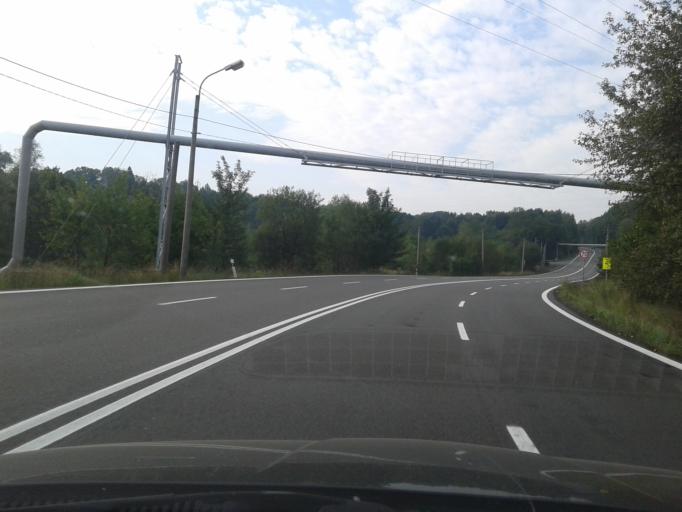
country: CZ
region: Moravskoslezsky
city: Orlova
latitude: 49.8333
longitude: 18.4369
